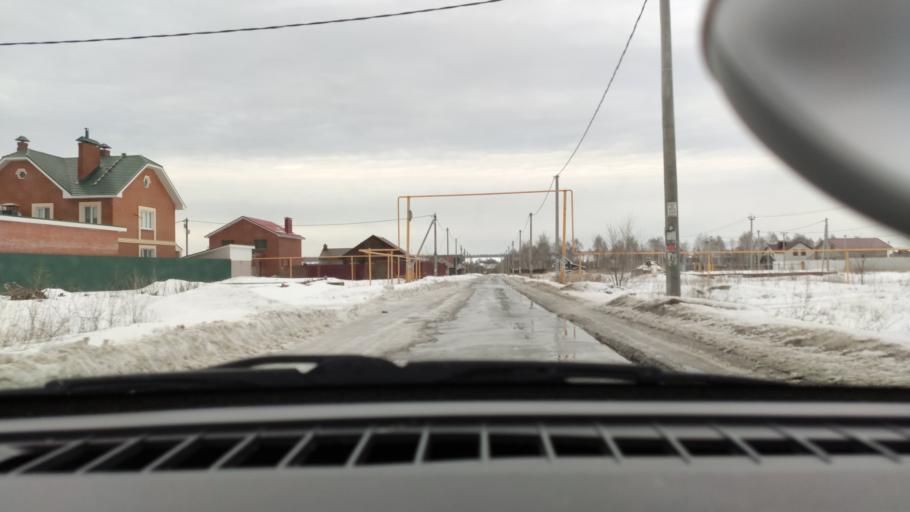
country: RU
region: Samara
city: Kurumoch
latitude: 53.4860
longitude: 50.0180
